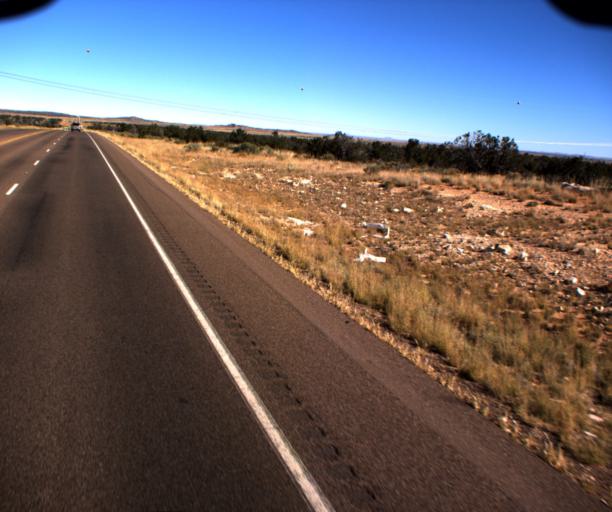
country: US
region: Arizona
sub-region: Navajo County
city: Snowflake
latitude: 34.6308
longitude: -110.0941
